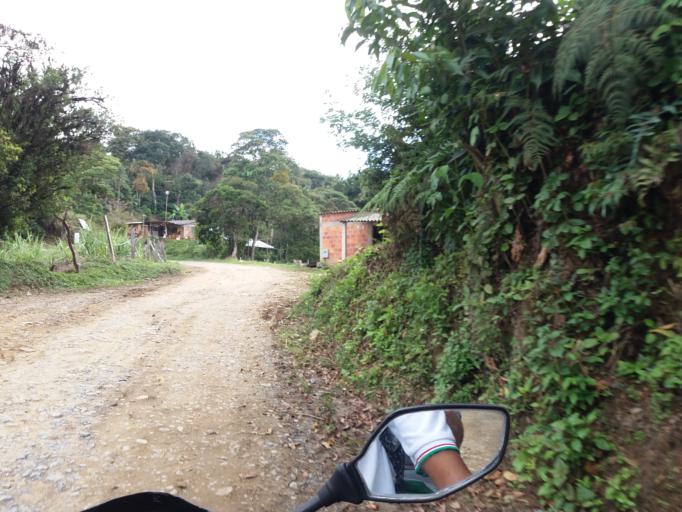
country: CO
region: Santander
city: Guepsa
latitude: 6.0038
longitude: -73.5438
